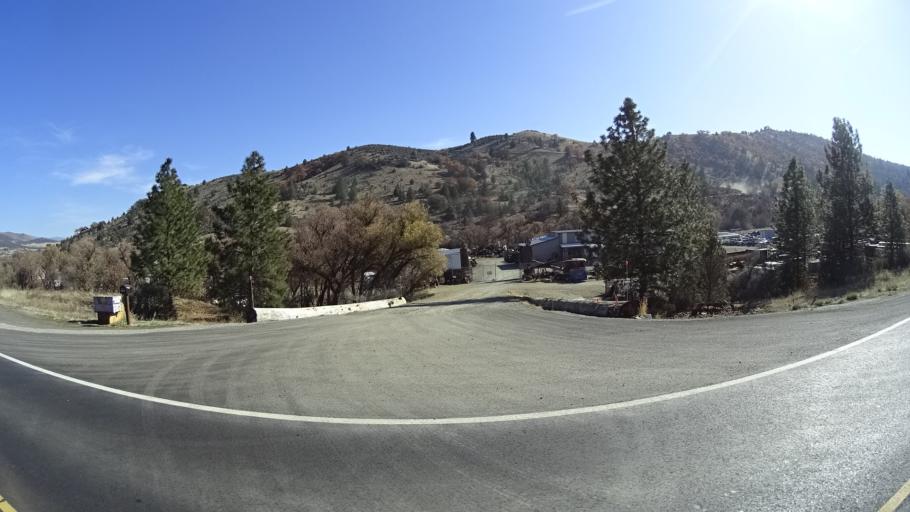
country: US
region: California
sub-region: Siskiyou County
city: Yreka
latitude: 41.7720
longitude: -122.6074
